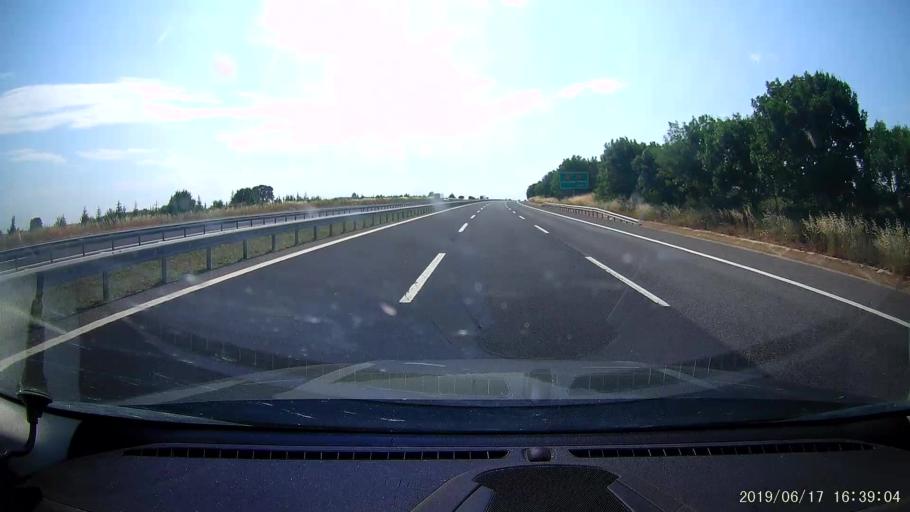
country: TR
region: Kirklareli
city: Luleburgaz
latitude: 41.4470
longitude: 27.4229
